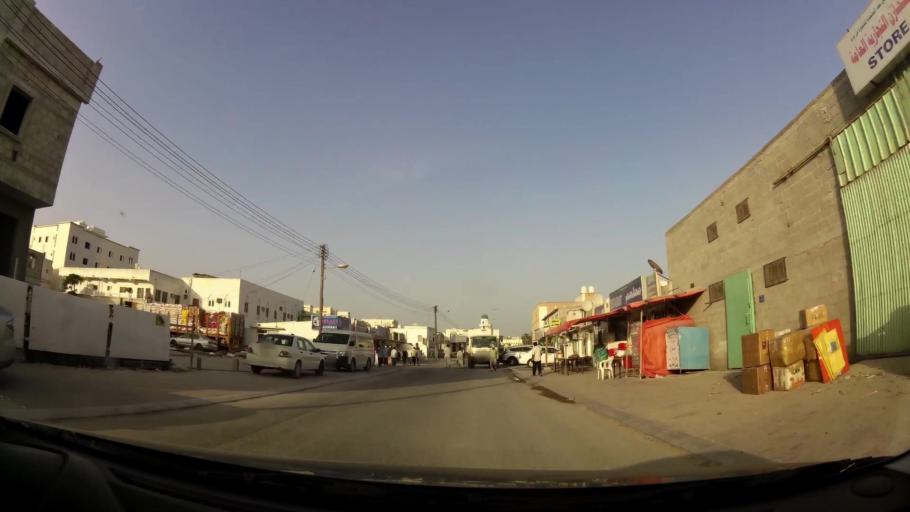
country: OM
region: Zufar
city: Salalah
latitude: 17.0126
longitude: 54.0988
